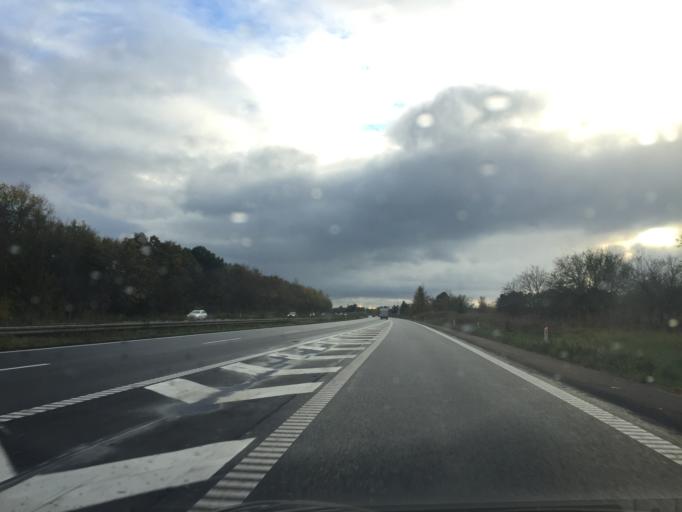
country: DK
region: Capital Region
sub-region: Fredensborg Kommune
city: Niva
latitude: 55.9641
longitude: 12.4870
